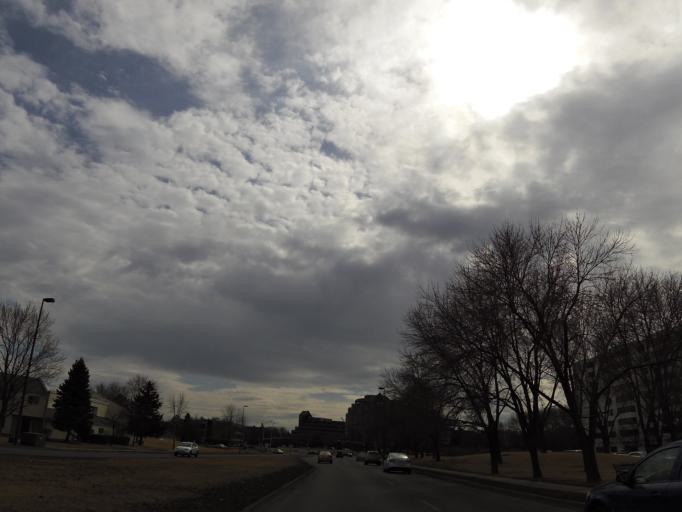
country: US
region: Minnesota
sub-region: Hennepin County
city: Bloomington
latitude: 44.8674
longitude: -93.3215
